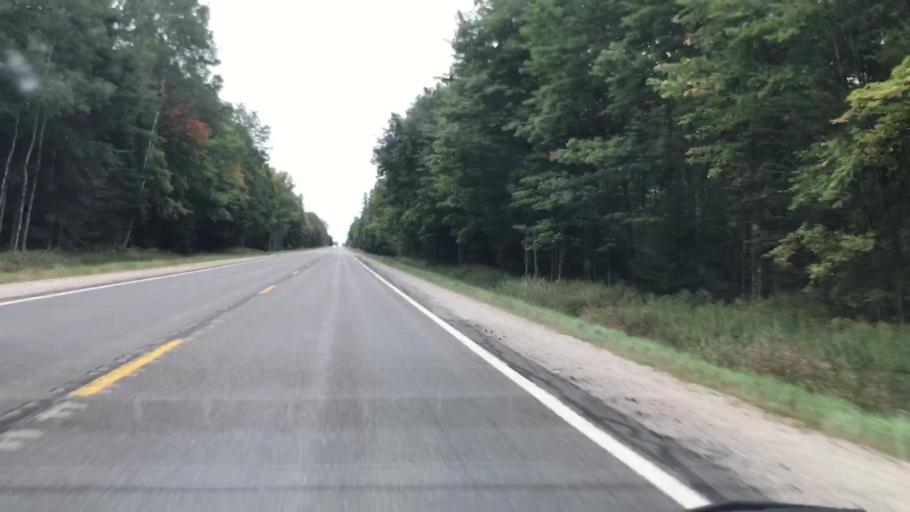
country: US
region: Michigan
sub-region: Luce County
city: Newberry
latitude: 46.2281
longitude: -85.5721
